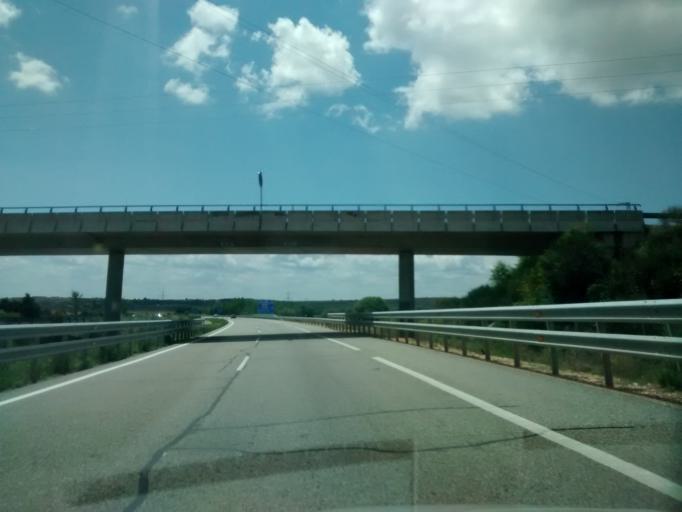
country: ES
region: Castille and Leon
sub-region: Provincia de Leon
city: Astorga
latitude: 42.4604
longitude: -6.0844
